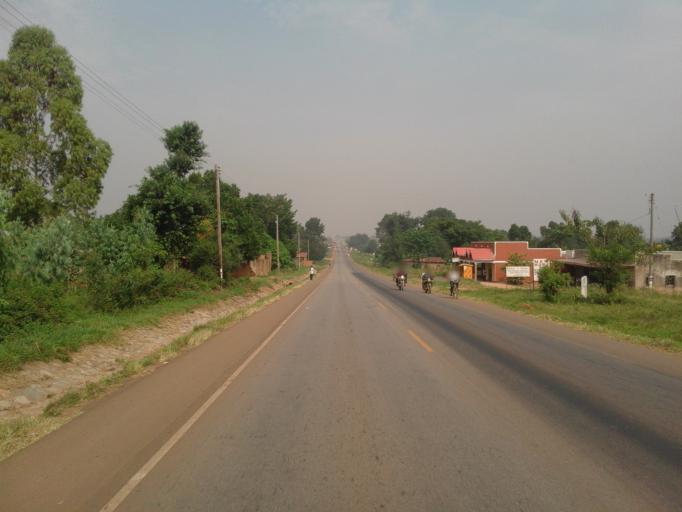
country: UG
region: Eastern Region
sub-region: Bugiri District
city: Bugiri
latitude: 0.5601
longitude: 33.7598
